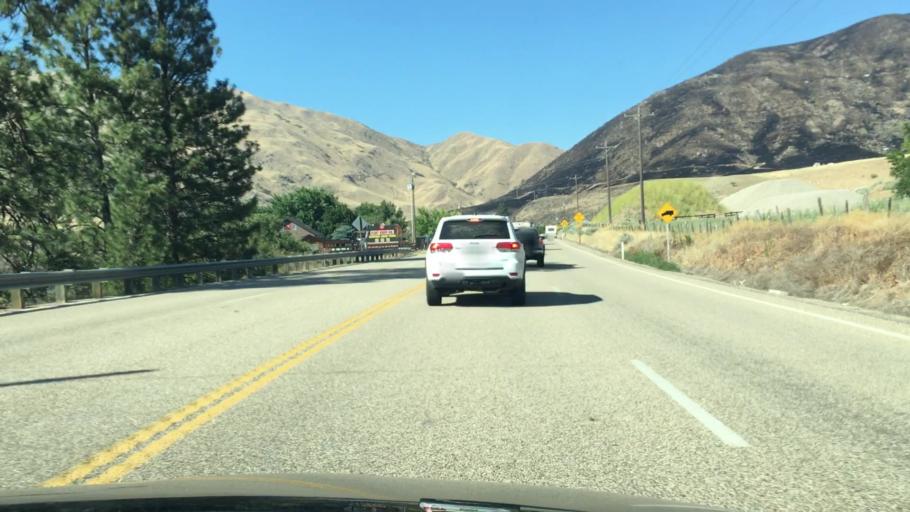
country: US
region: Idaho
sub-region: Gem County
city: Emmett
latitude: 43.9949
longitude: -116.1868
